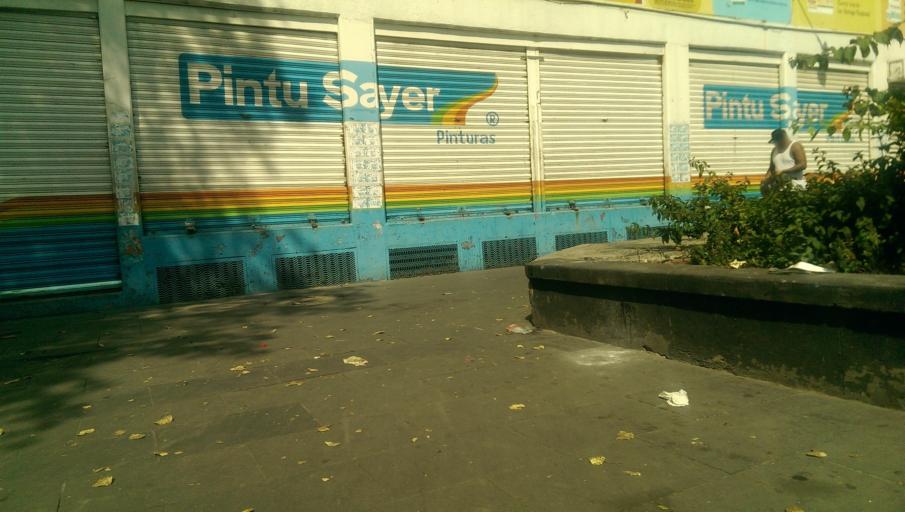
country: MX
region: Mexico City
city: Mexico City
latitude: 19.4319
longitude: -99.1235
